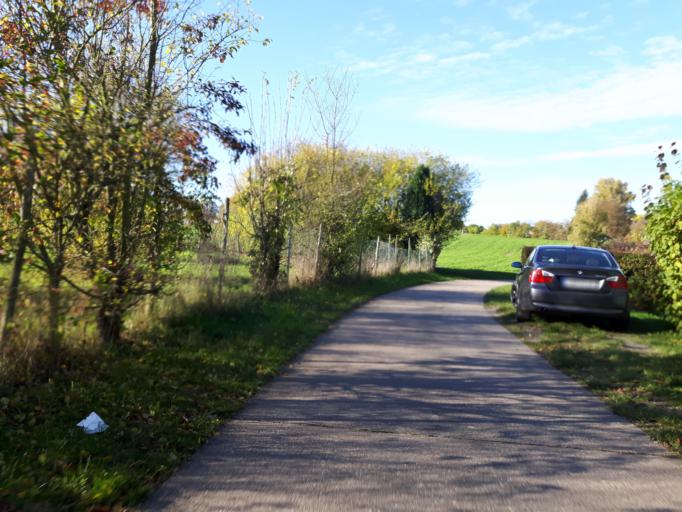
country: DE
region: Baden-Wuerttemberg
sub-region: Regierungsbezirk Stuttgart
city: Flein
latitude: 49.1133
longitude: 9.1976
